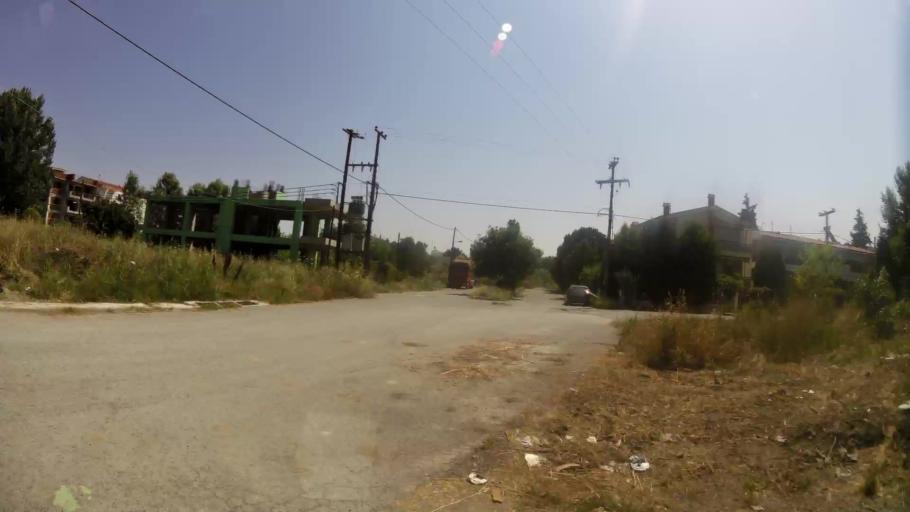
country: GR
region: Central Macedonia
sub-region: Nomos Thessalonikis
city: Neoi Epivates
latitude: 40.5017
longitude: 22.9033
